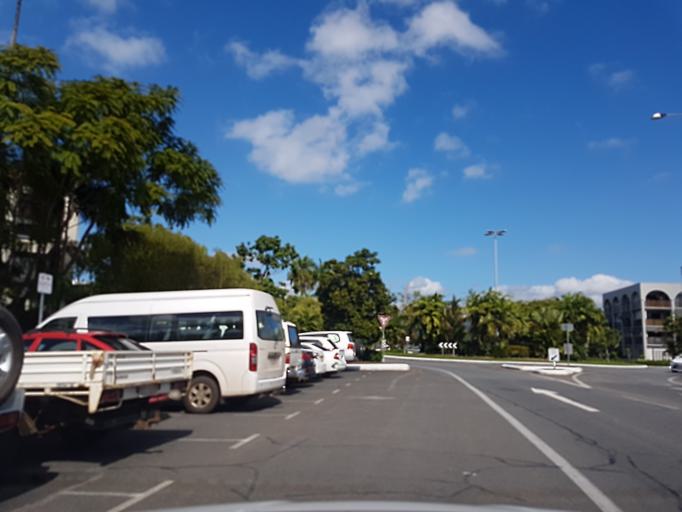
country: AU
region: Queensland
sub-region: Cairns
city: Cairns
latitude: -16.9143
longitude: 145.7715
